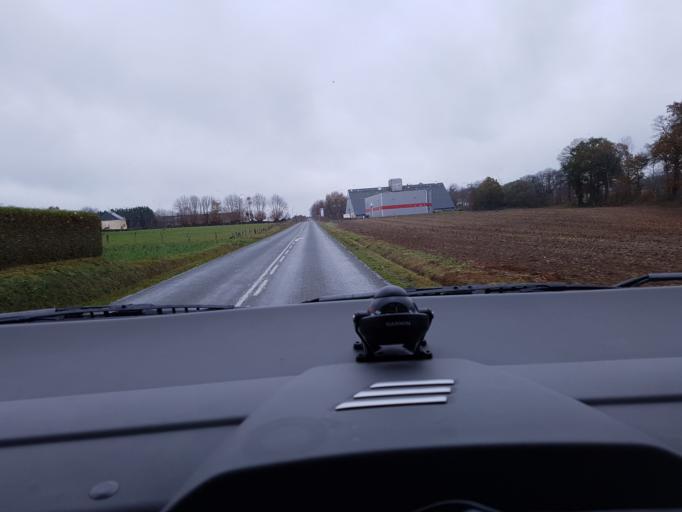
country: FR
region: Pays de la Loire
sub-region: Departement de la Mayenne
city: Gorron
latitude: 48.4017
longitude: -0.8301
